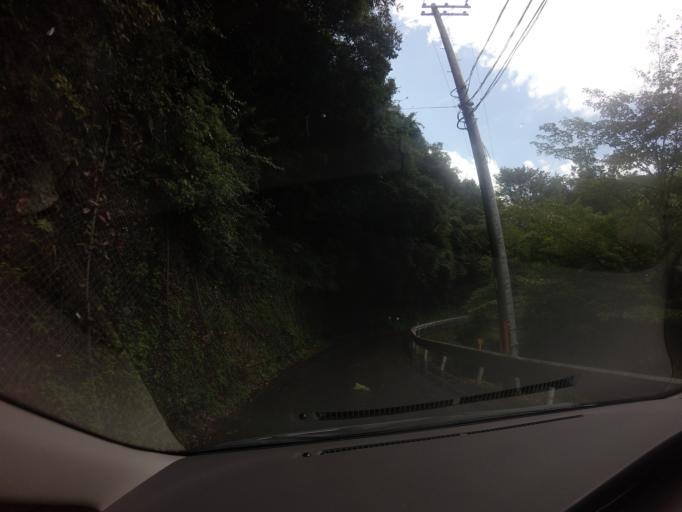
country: JP
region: Wakayama
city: Shingu
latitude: 33.9637
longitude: 135.8478
